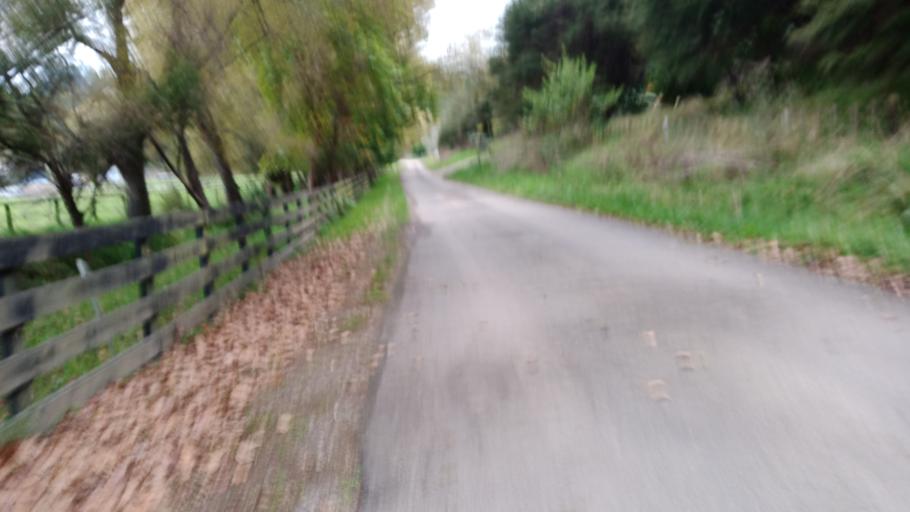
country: NZ
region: Gisborne
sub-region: Gisborne District
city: Gisborne
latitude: -38.6448
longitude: 178.0351
